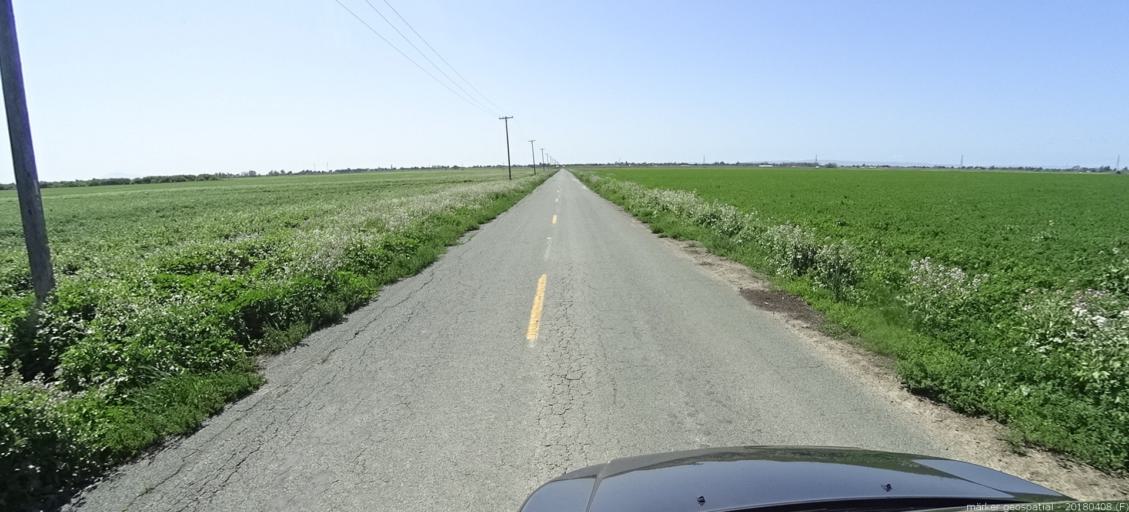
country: US
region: California
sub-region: Sacramento County
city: Walnut Grove
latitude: 38.3103
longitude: -121.5338
